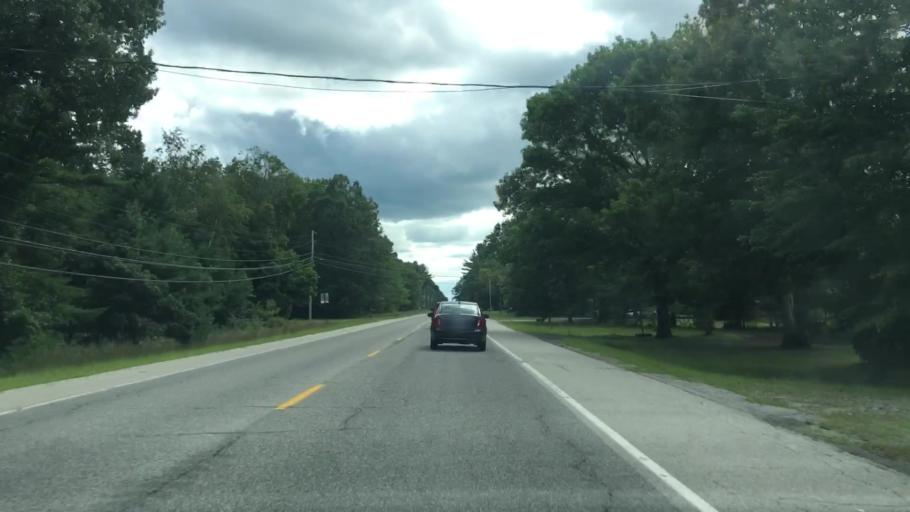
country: US
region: Maine
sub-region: York County
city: North Berwick
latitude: 43.3425
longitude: -70.7317
